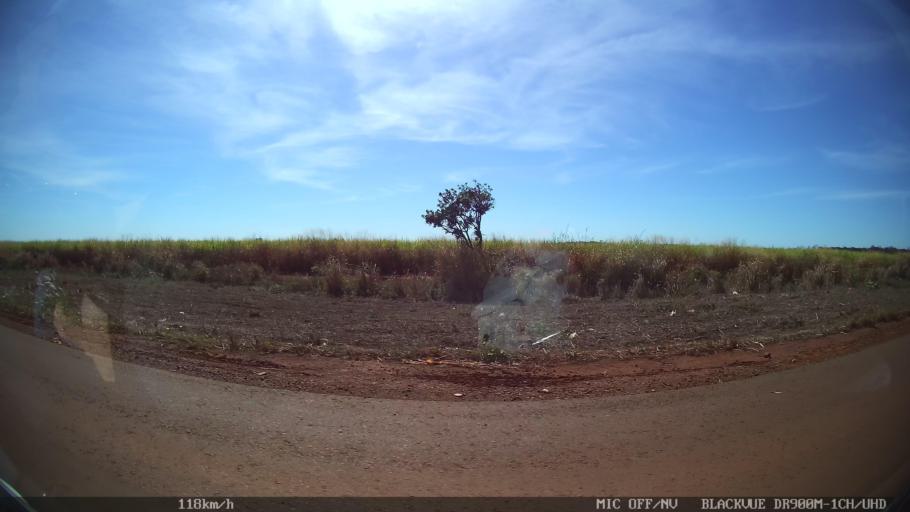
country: BR
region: Sao Paulo
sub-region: Sao Joaquim Da Barra
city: Sao Joaquim da Barra
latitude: -20.5586
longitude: -47.7016
